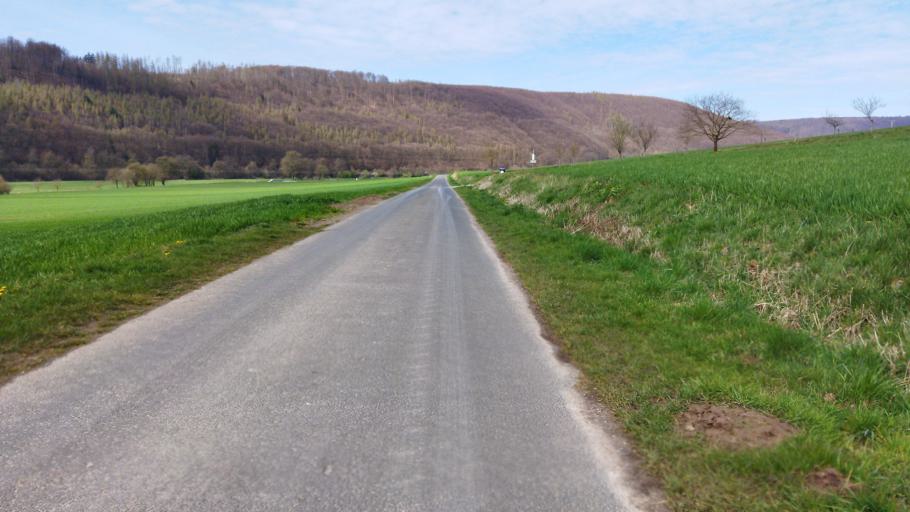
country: DE
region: Lower Saxony
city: Bad Karlshafen
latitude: 51.6327
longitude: 9.5019
